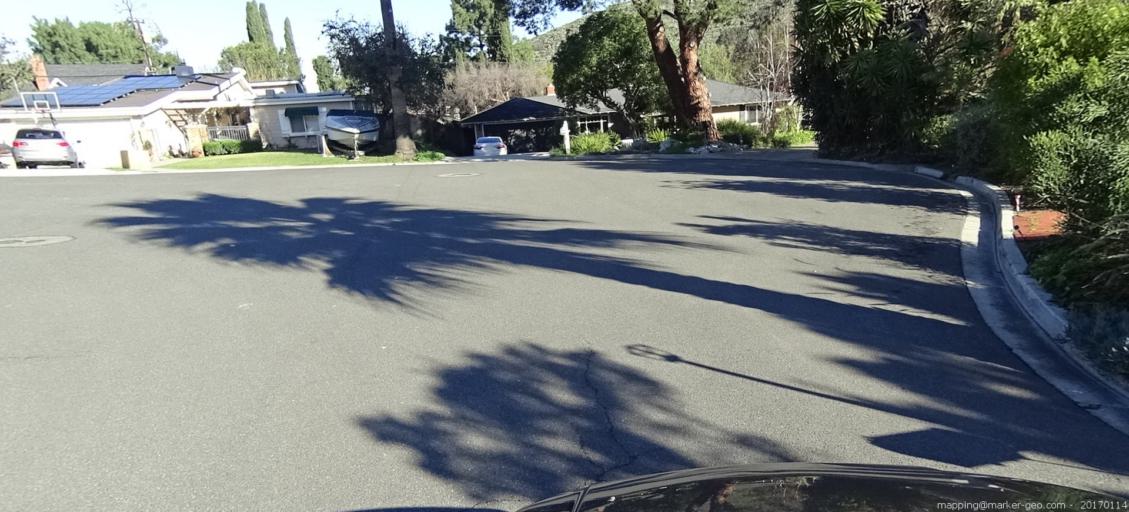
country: US
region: California
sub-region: Orange County
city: North Tustin
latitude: 33.7801
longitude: -117.7953
